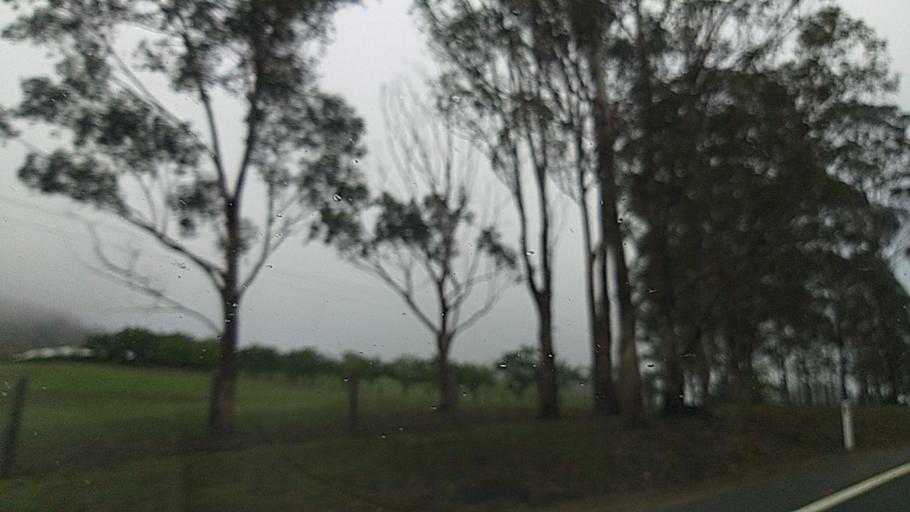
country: AU
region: New South Wales
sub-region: Camden
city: Camden South
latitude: -34.1247
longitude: 150.6999
